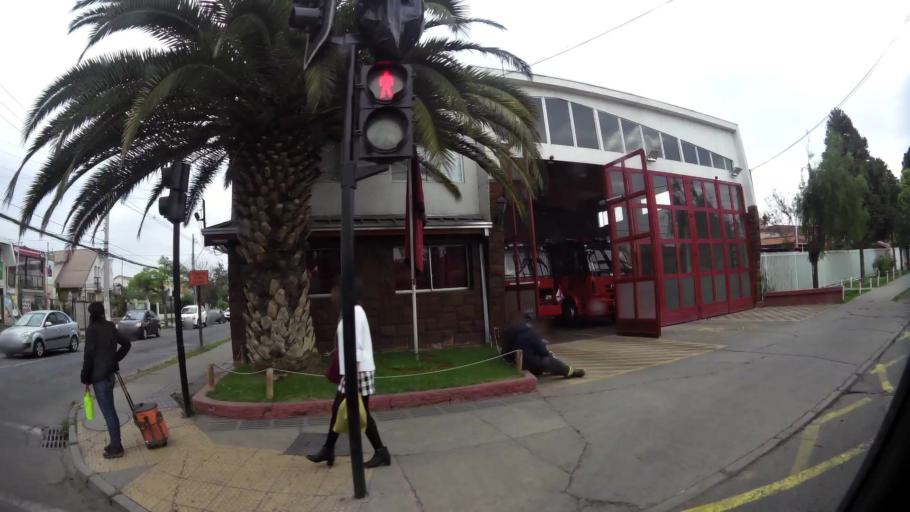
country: CL
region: Santiago Metropolitan
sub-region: Provincia de Santiago
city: Lo Prado
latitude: -33.5070
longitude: -70.7530
